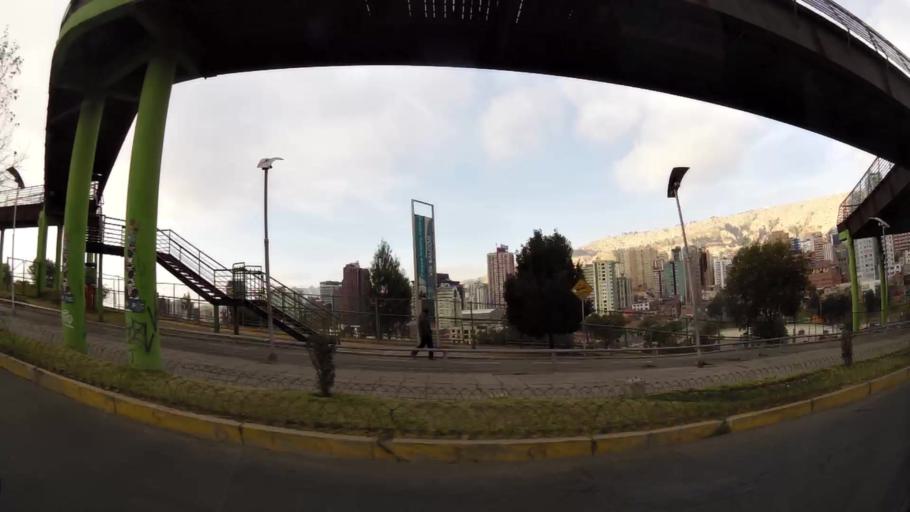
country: BO
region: La Paz
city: La Paz
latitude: -16.5025
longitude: -68.1261
